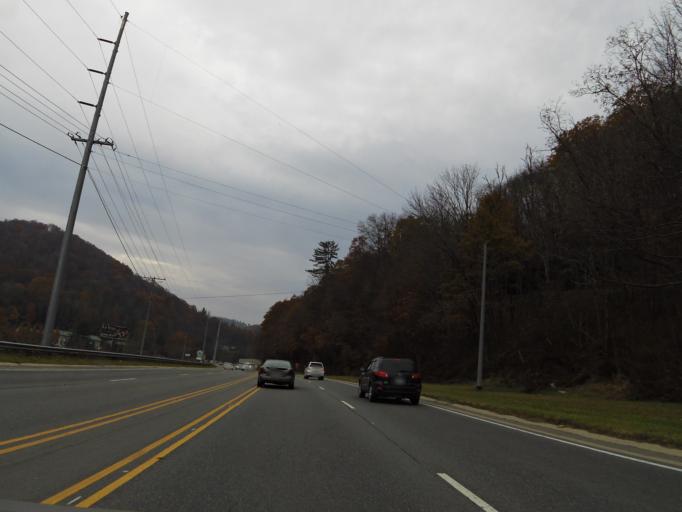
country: US
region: North Carolina
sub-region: Watauga County
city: Blowing Rock
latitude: 36.1577
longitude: -81.6466
